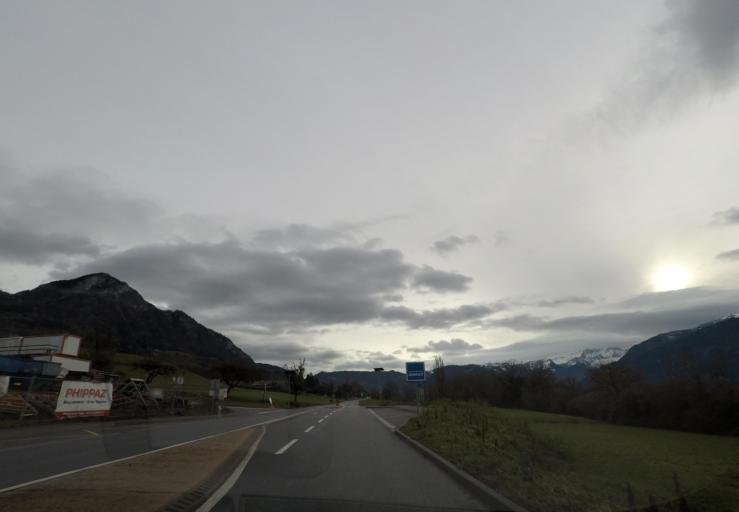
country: FR
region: Rhone-Alpes
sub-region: Departement de la Haute-Savoie
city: Marignier
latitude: 46.0908
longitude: 6.5188
